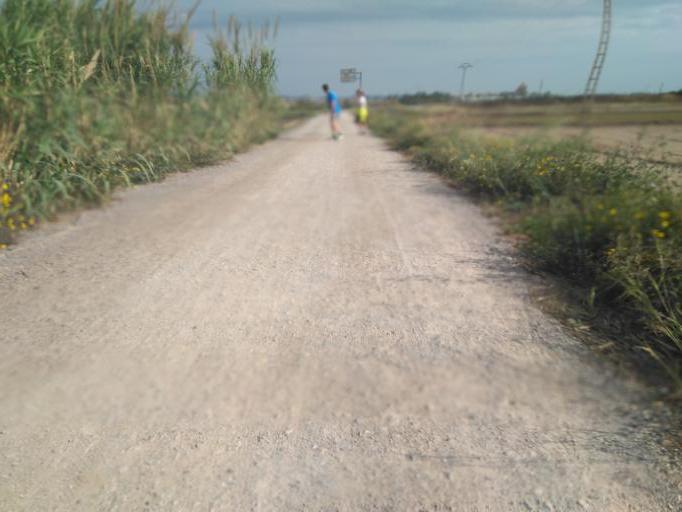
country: ES
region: Valencia
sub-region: Provincia de Valencia
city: Alboraya
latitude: 39.4967
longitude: -0.3256
